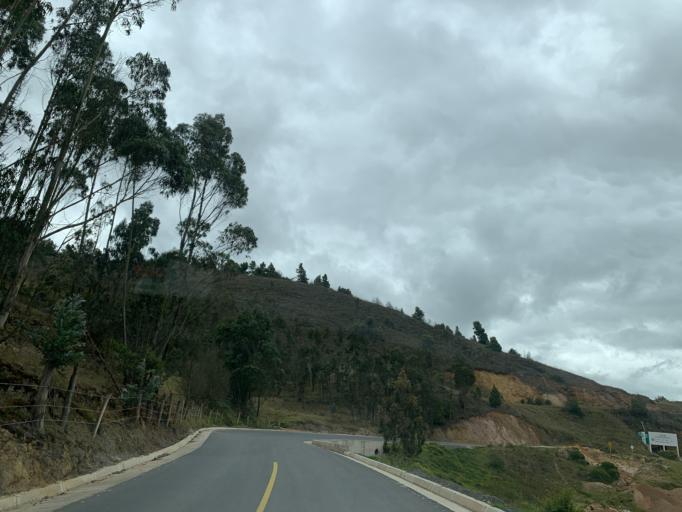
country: CO
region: Boyaca
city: Tunja
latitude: 5.5305
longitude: -73.3258
